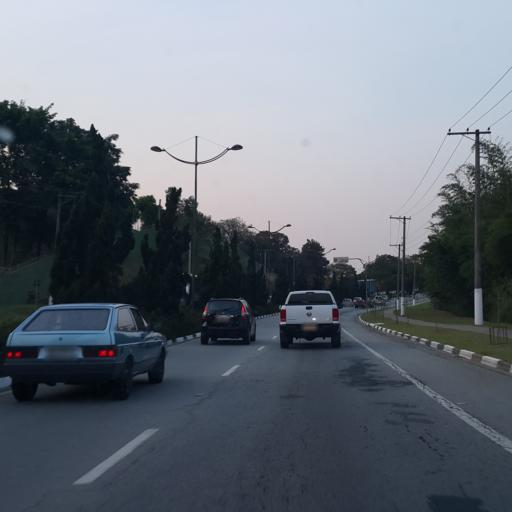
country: BR
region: Sao Paulo
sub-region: Vinhedo
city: Vinhedo
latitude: -23.0509
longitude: -46.9860
